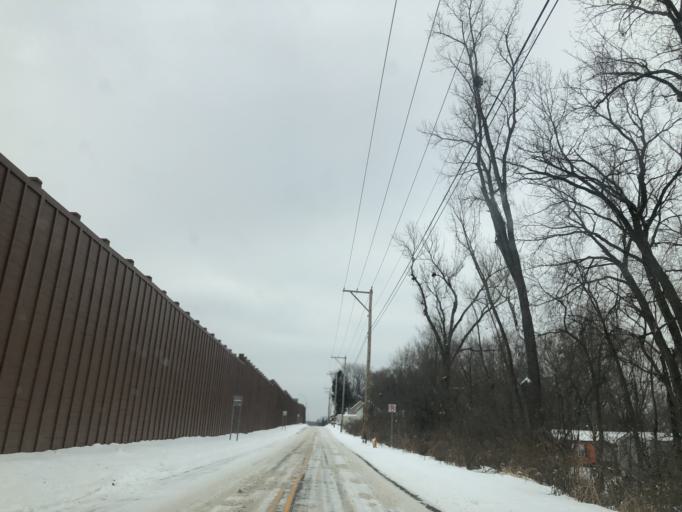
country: US
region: Minnesota
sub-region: Ramsey County
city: New Brighton
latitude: 45.0832
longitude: -93.1815
